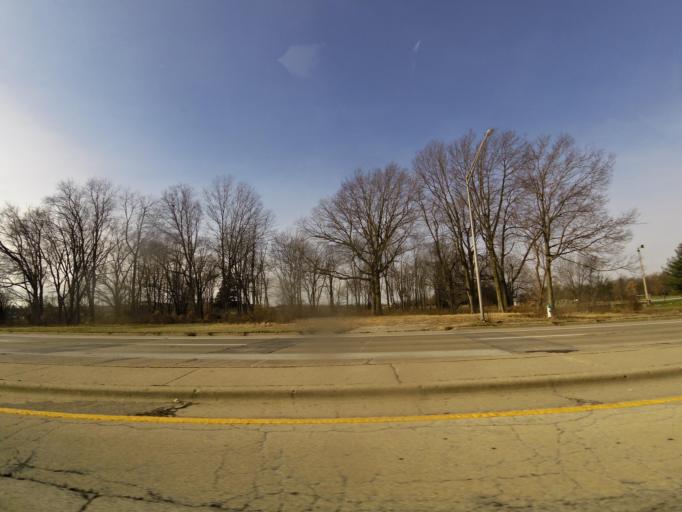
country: US
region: Illinois
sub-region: Macon County
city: Forsyth
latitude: 39.9307
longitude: -88.9555
